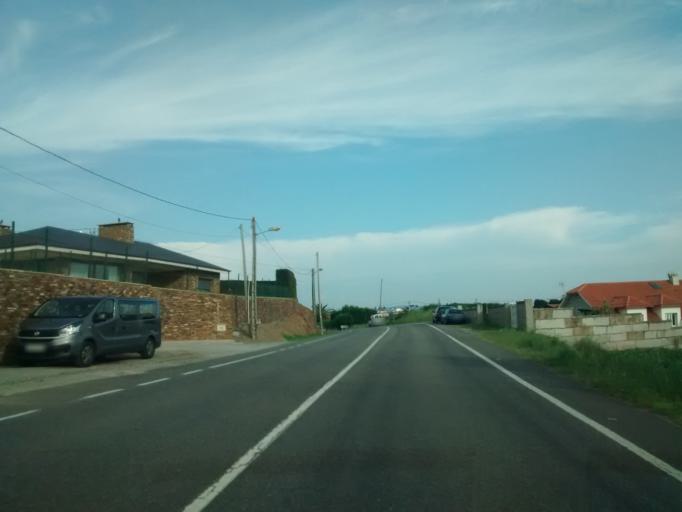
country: ES
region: Galicia
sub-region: Provincia de Pontevedra
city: Sanxenxo
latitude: 42.4118
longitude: -8.8619
